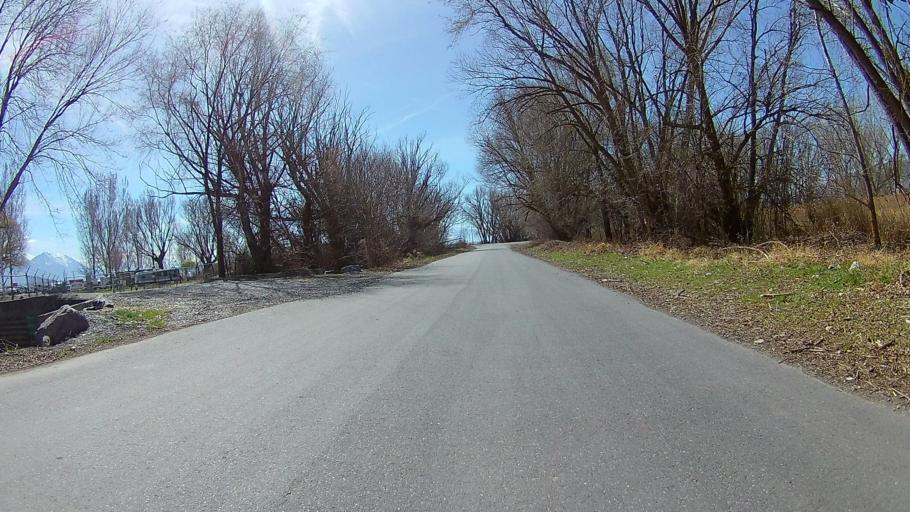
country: US
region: Utah
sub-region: Utah County
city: American Fork
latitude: 40.3452
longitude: -111.8017
